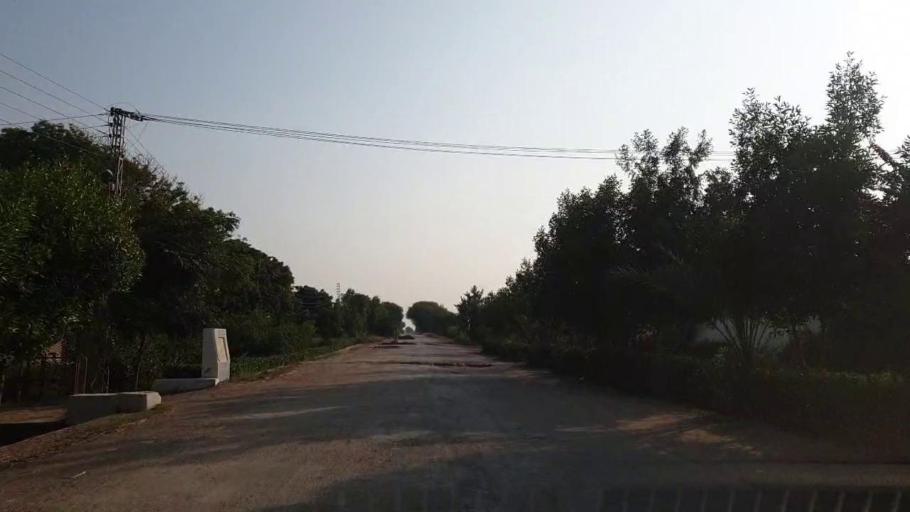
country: PK
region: Sindh
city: Bulri
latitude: 24.9858
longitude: 68.3920
